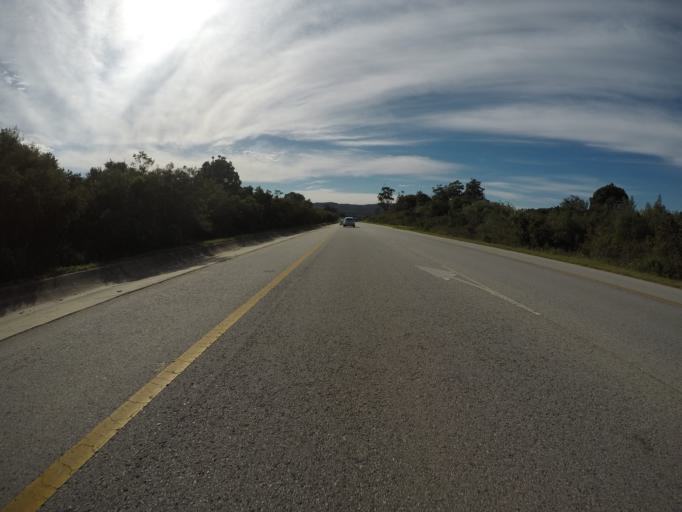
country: ZA
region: Eastern Cape
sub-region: Cacadu District Municipality
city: Jeffrey's Bay
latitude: -33.8938
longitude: 25.1301
